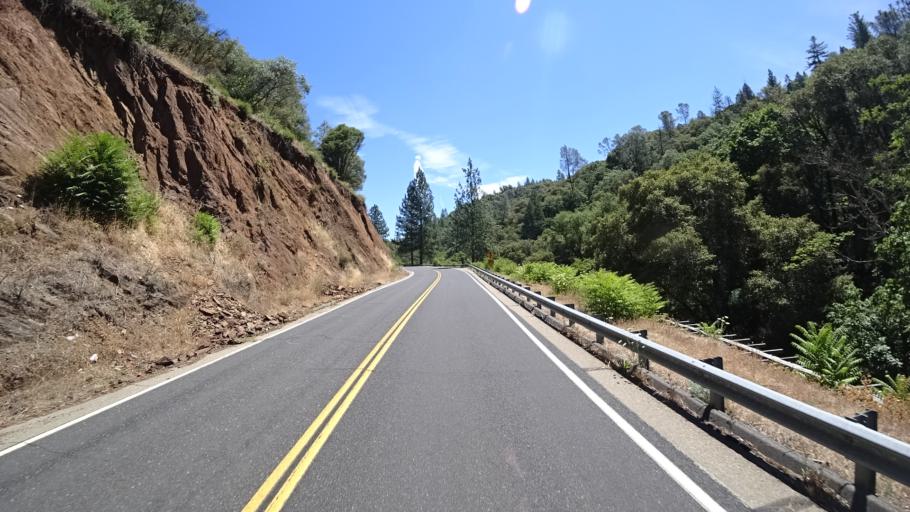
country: US
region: California
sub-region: Calaveras County
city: Murphys
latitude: 38.1313
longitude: -120.4843
